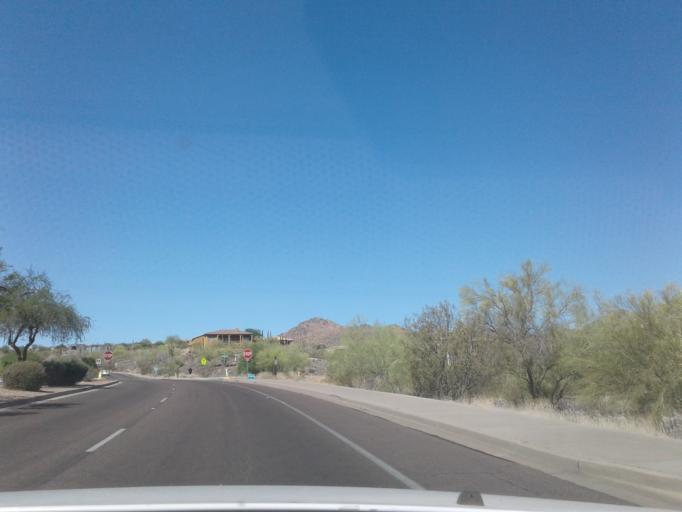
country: US
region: Arizona
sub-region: Maricopa County
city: Fountain Hills
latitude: 33.6142
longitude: -111.7358
